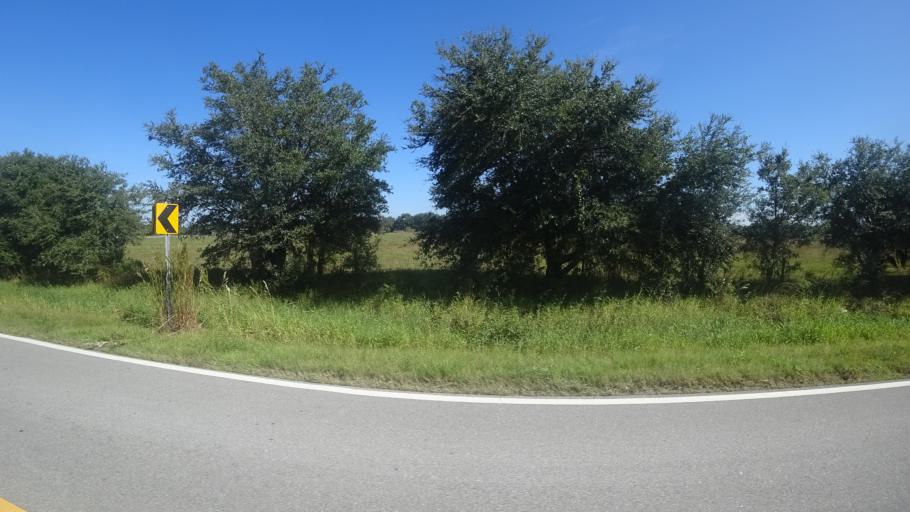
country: US
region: Florida
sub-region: Sarasota County
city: Lake Sarasota
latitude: 27.2901
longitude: -82.2343
